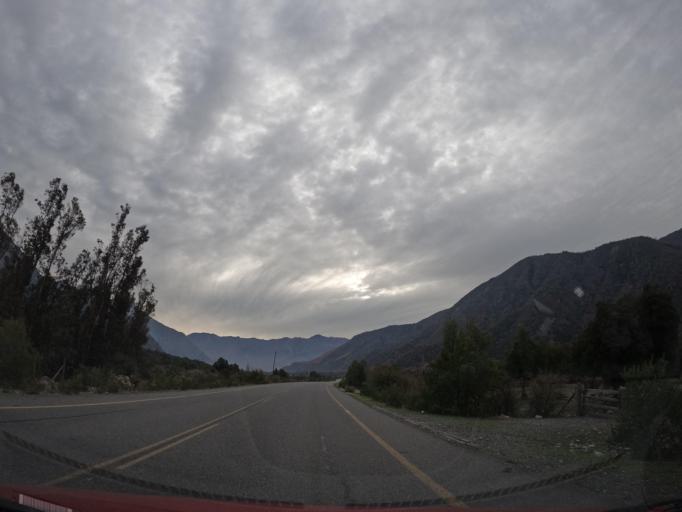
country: CL
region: Maule
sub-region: Provincia de Linares
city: Colbun
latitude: -35.7250
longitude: -71.0254
